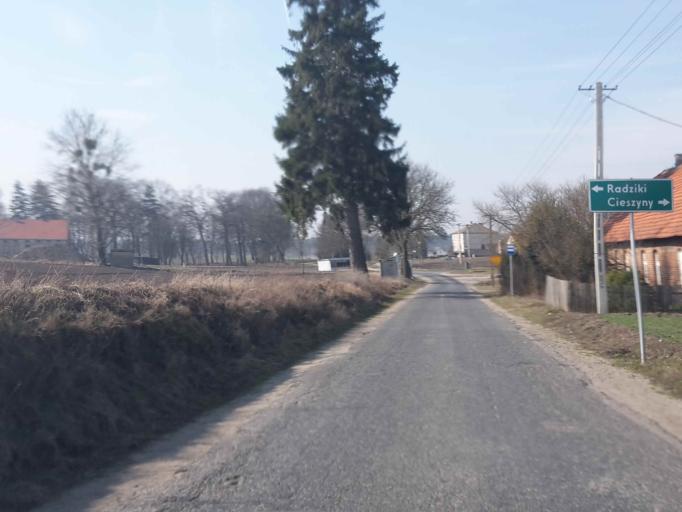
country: PL
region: Kujawsko-Pomorskie
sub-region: Powiat rypinski
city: Wapielsk
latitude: 53.2015
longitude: 19.2341
